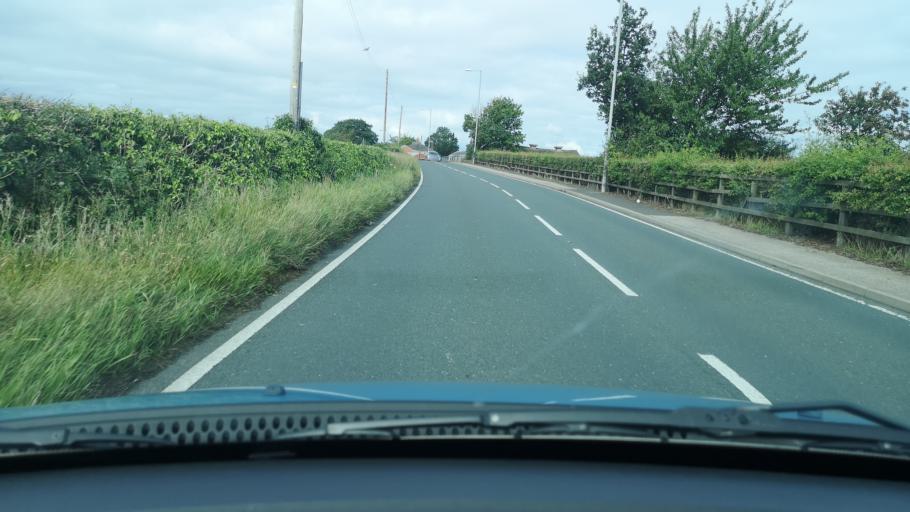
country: GB
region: England
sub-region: City and Borough of Wakefield
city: Middlestown
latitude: 53.6600
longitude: -1.5898
